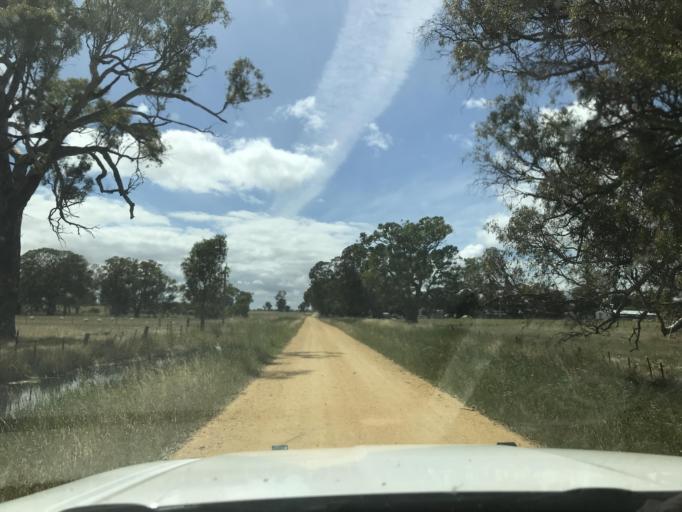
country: AU
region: South Australia
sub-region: Naracoorte and Lucindale
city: Naracoorte
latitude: -37.0196
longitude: 141.1038
